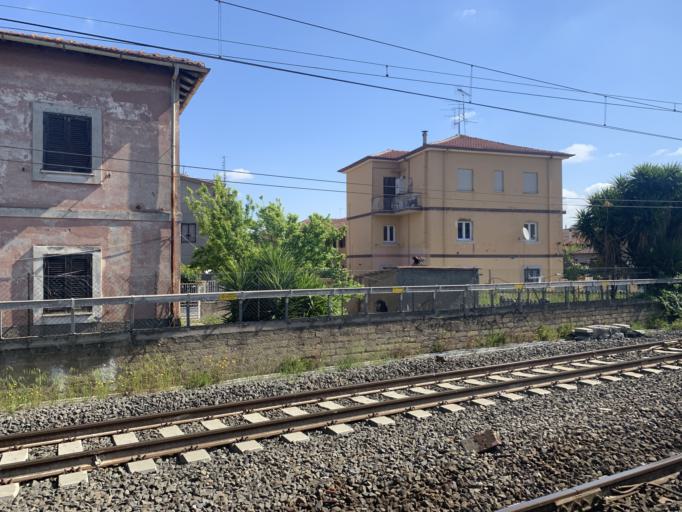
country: IT
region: Latium
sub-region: Citta metropolitana di Roma Capitale
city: Ciampino
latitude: 41.8058
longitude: 12.5956
